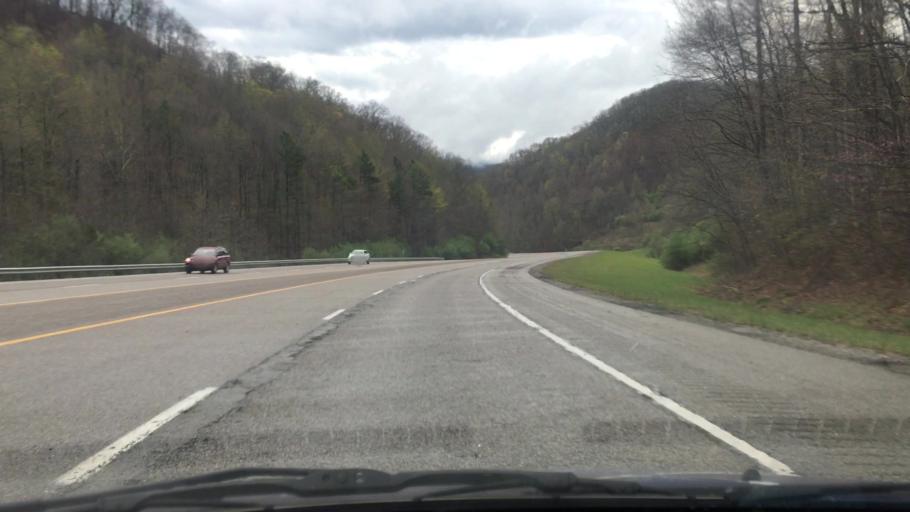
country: US
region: Kentucky
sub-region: Letcher County
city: Jenkins
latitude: 37.2102
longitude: -82.6234
